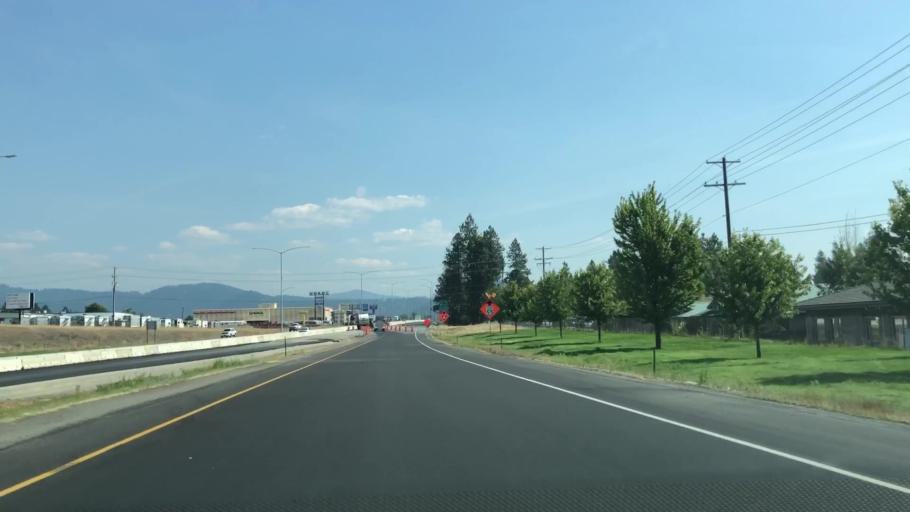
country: US
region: Idaho
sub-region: Kootenai County
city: Coeur d'Alene
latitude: 47.6991
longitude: -116.8052
